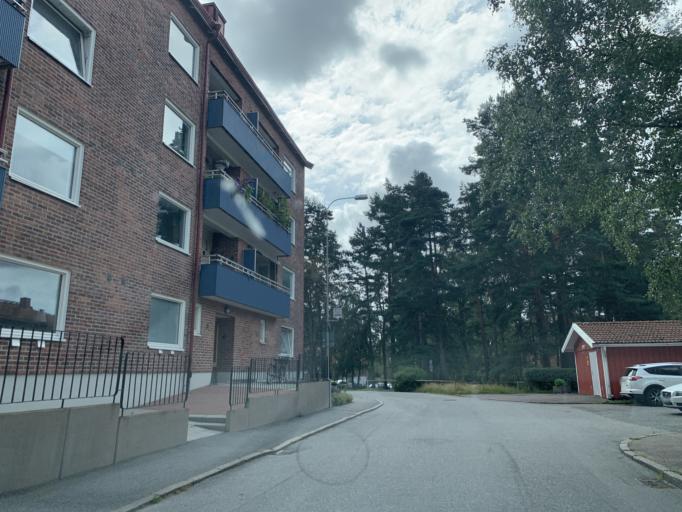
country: SE
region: Vaestra Goetaland
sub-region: Goteborg
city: Eriksbo
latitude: 57.7557
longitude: 12.0379
